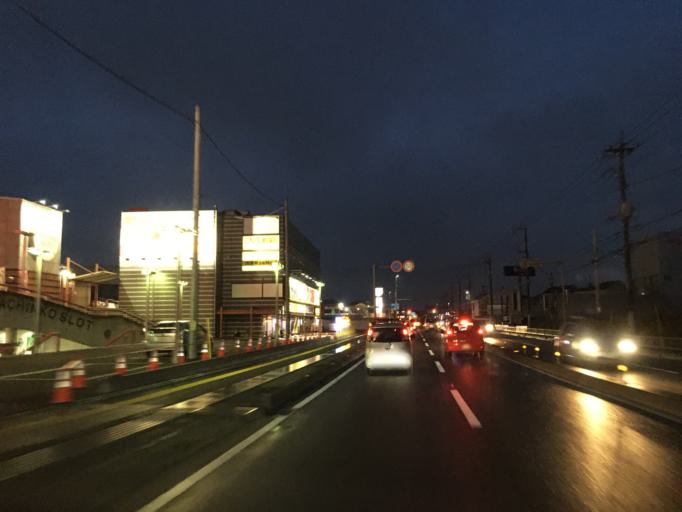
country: JP
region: Saitama
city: Shiki
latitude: 35.8070
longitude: 139.5507
